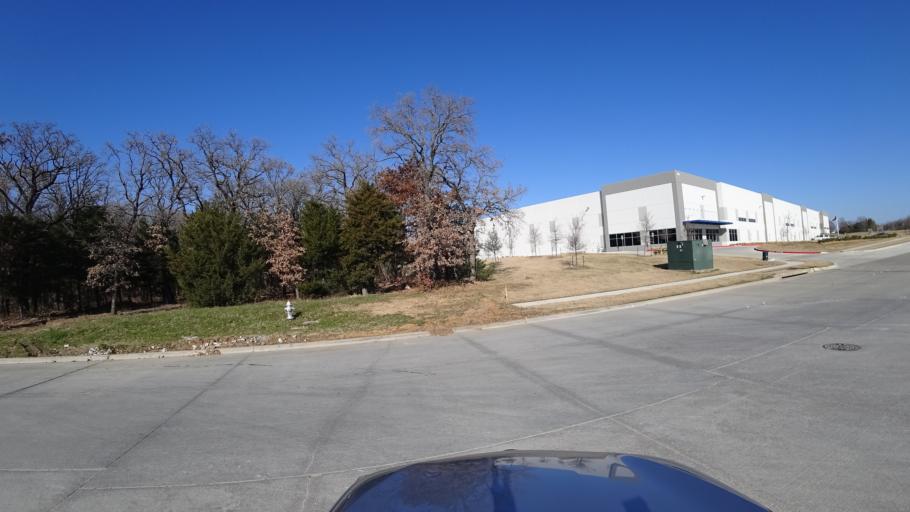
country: US
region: Texas
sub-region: Dallas County
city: Coppell
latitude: 32.9944
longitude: -96.9999
